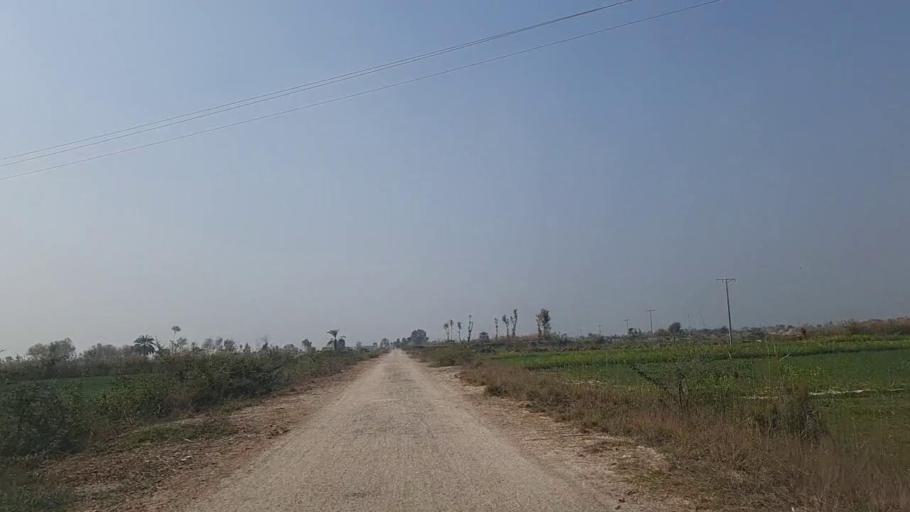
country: PK
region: Sindh
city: Daur
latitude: 26.4487
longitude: 68.4480
